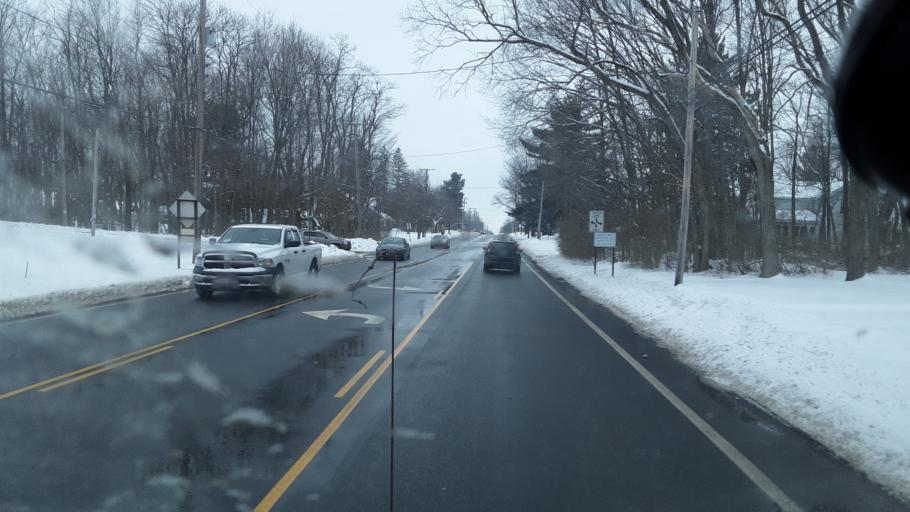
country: US
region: Ohio
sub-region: Richland County
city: Ontario
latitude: 40.7590
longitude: -82.5748
